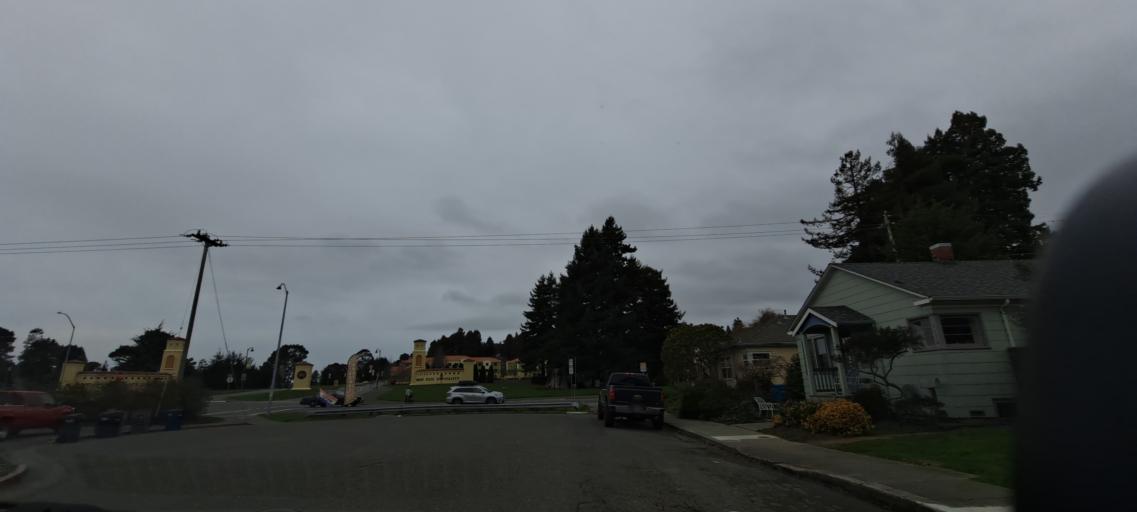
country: US
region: California
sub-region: Humboldt County
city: Arcata
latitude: 40.8717
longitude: -124.0813
